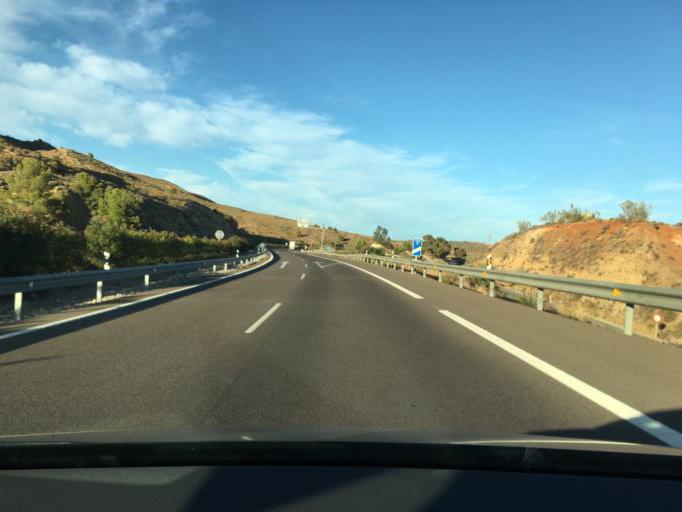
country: ES
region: Andalusia
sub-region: Provincia de Almeria
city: Bedar
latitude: 37.1442
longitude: -1.9899
